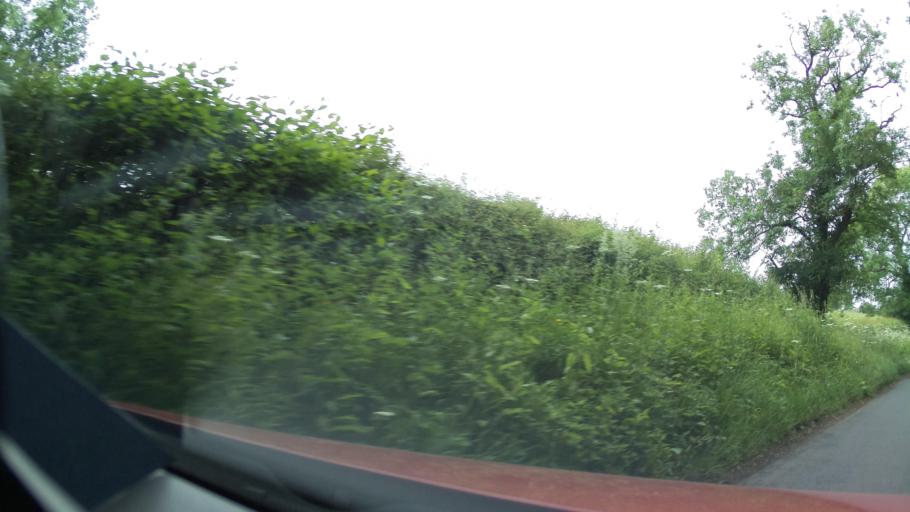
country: GB
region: England
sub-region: Leicestershire
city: Melton Mowbray
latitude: 52.7120
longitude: -0.8323
